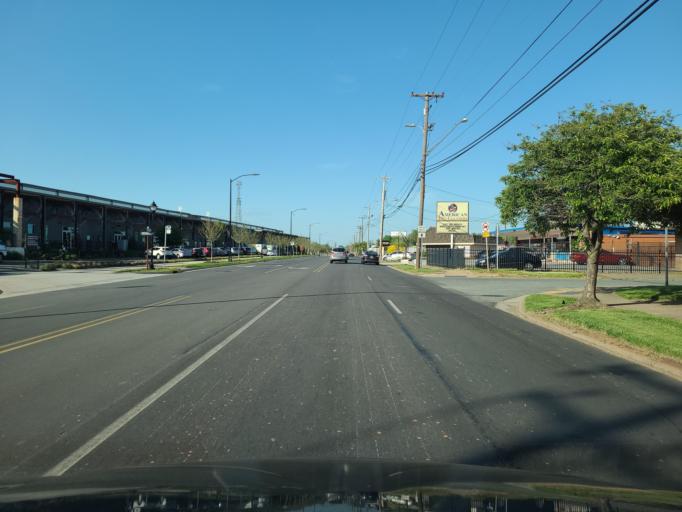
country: US
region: North Carolina
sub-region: Mecklenburg County
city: Charlotte
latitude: 35.2446
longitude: -80.8320
